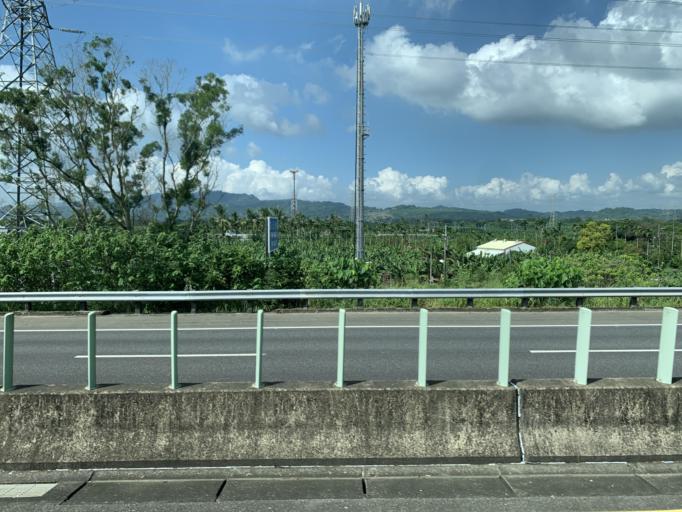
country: TW
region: Taiwan
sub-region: Pingtung
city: Pingtung
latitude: 22.8544
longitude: 120.4950
